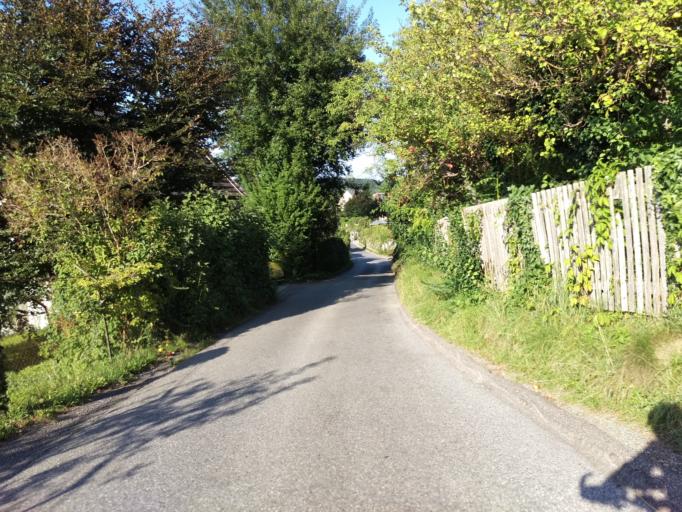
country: AT
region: Styria
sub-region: Graz Stadt
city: Mariatrost
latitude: 47.0707
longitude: 15.4929
